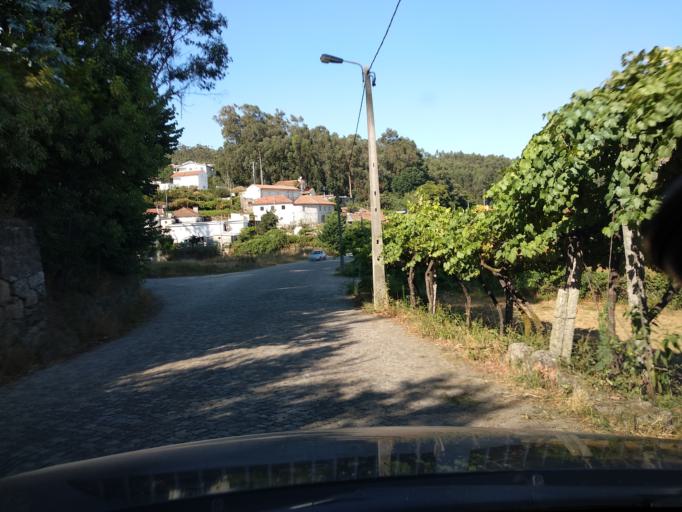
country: PT
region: Porto
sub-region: Paredes
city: Madalena
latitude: 41.2126
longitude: -8.3618
